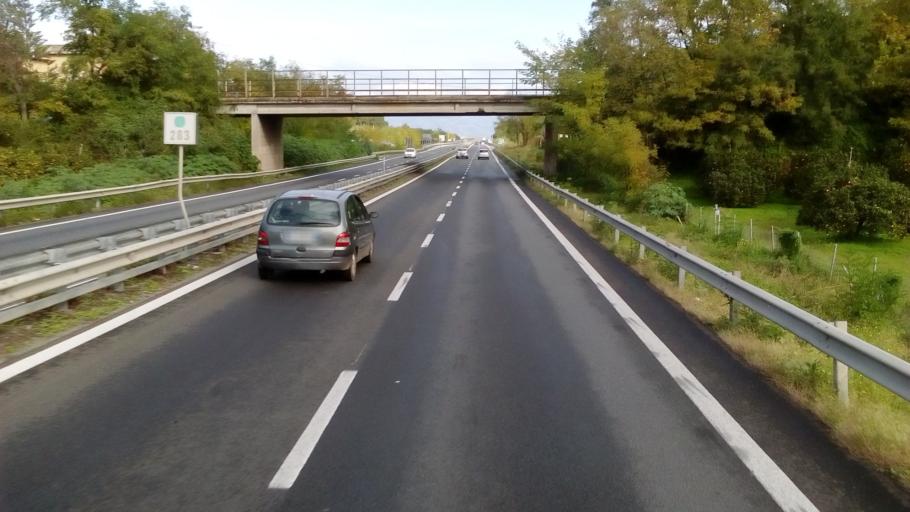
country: IT
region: Calabria
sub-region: Provincia di Vibo-Valentia
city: Pizzo
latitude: 38.7771
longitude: 16.2159
